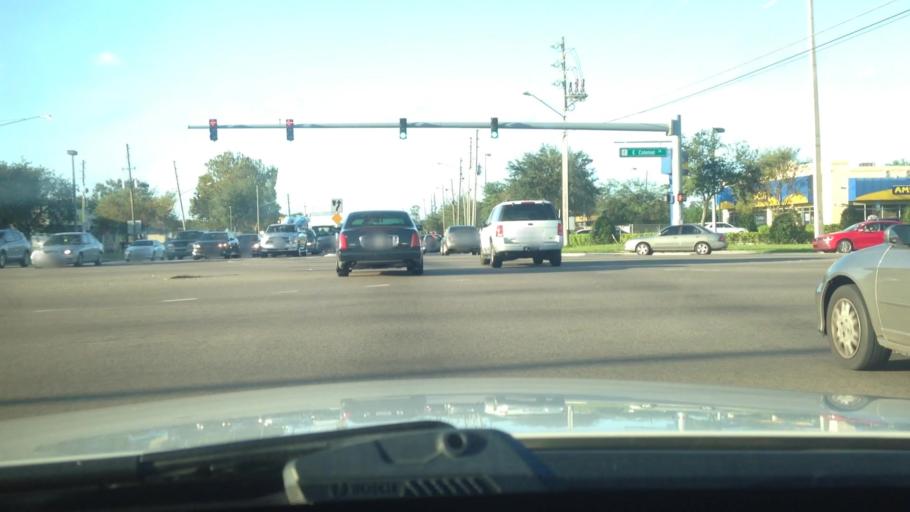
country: US
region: Florida
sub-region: Orange County
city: Union Park
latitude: 28.5680
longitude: -81.2860
